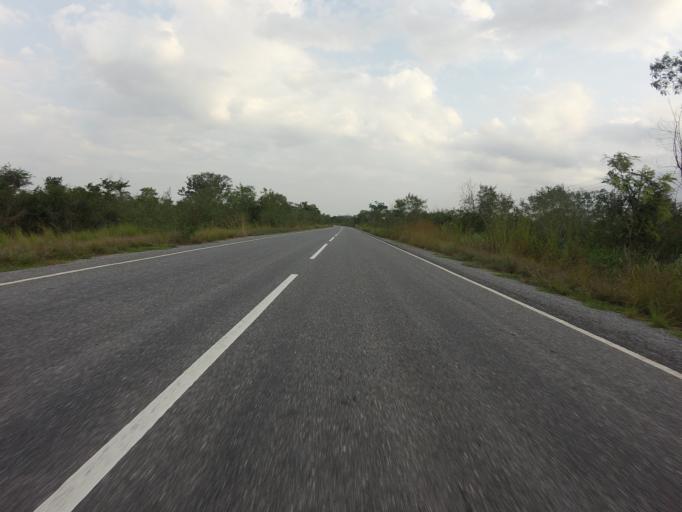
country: GH
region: Volta
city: Ho
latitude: 6.3457
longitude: 0.5382
